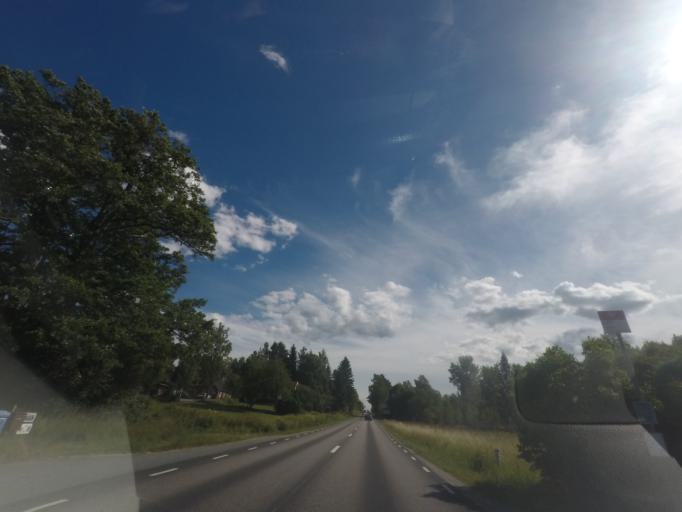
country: SE
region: Stockholm
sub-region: Norrtalje Kommun
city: Arno
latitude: 59.9986
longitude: 18.8022
